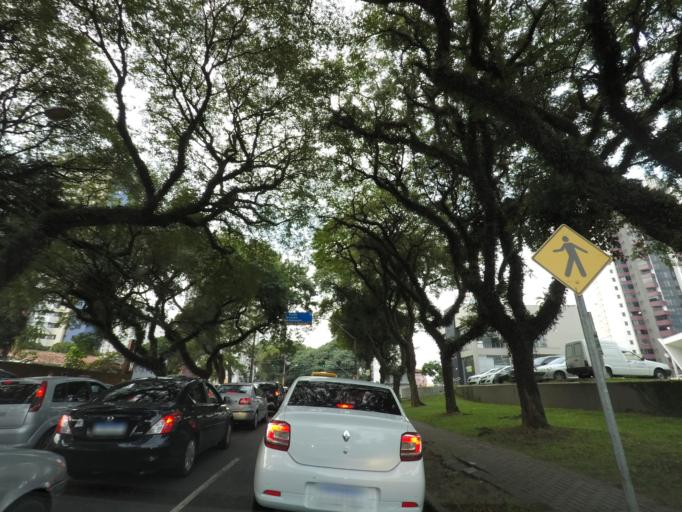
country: BR
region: Parana
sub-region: Curitiba
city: Curitiba
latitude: -25.4522
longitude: -49.2906
